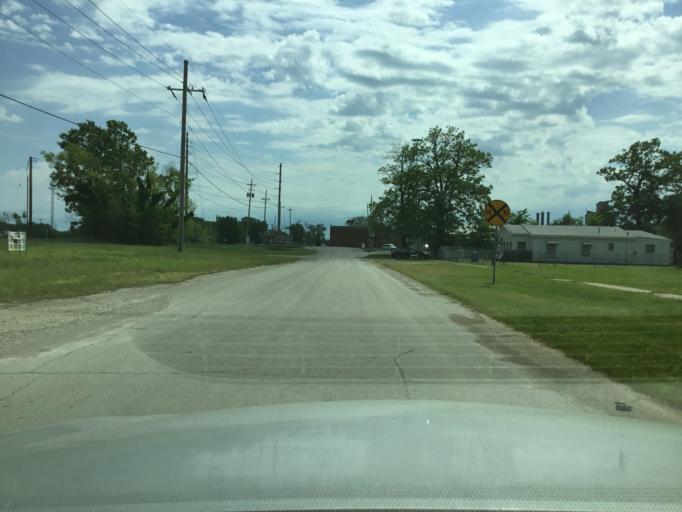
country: US
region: Kansas
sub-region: Montgomery County
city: Coffeyville
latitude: 37.0288
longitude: -95.6261
